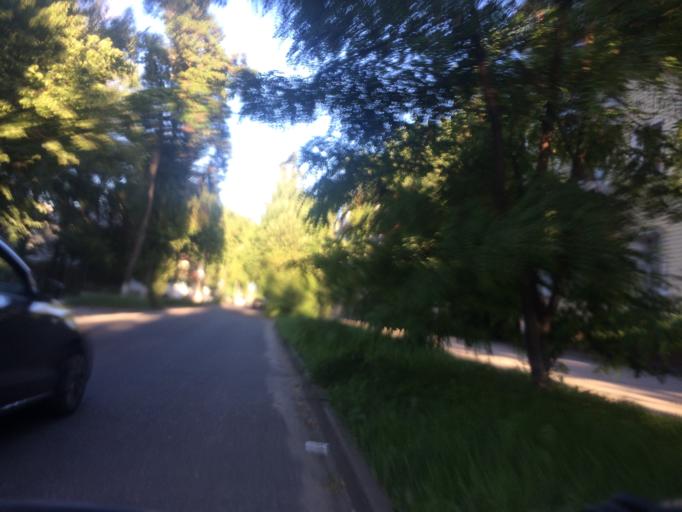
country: RU
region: Kursk
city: Kursk
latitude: 51.6724
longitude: 36.1497
